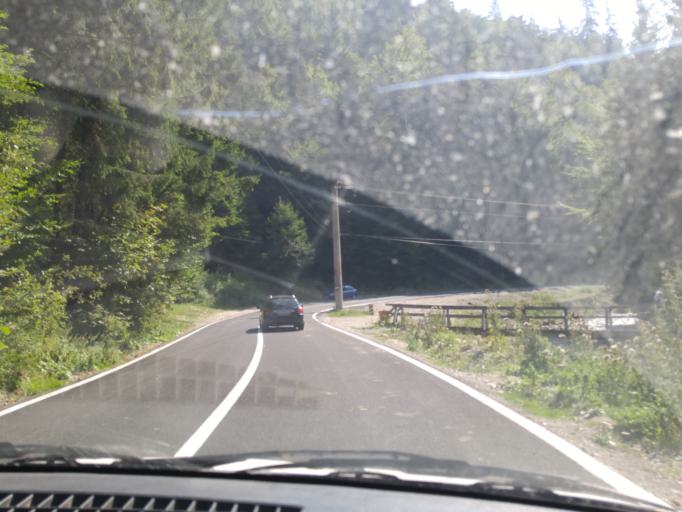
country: RO
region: Brasov
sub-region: Comuna Fundata
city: Fundata
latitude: 45.4569
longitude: 25.3146
